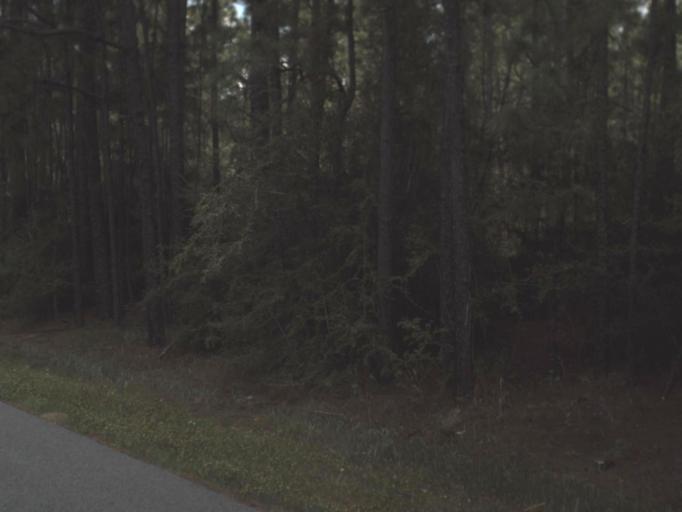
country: US
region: Florida
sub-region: Escambia County
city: Molino
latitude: 30.8152
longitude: -87.4296
